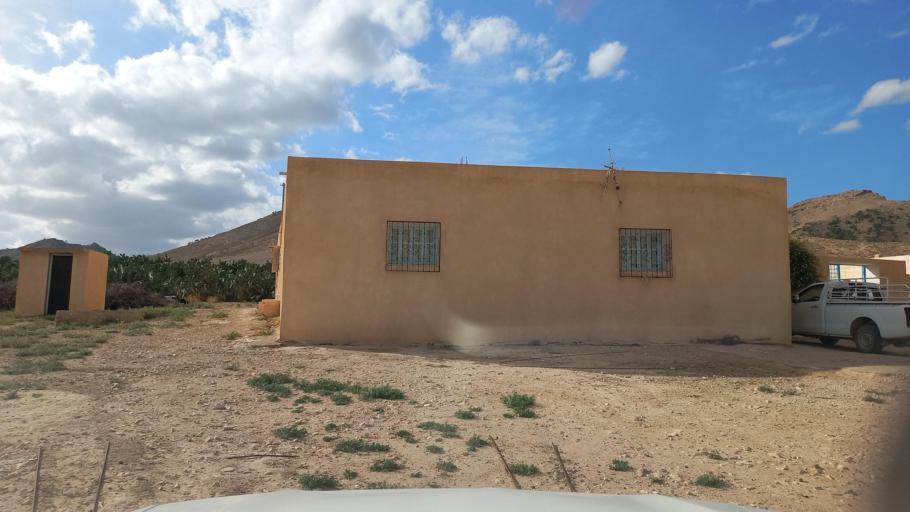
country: TN
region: Al Qasrayn
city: Sbiba
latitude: 35.4557
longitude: 9.0740
